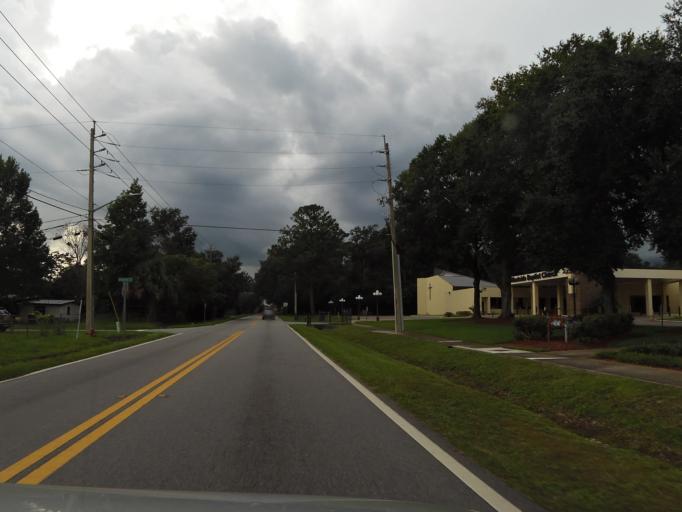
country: US
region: Florida
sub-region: Clay County
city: Bellair-Meadowbrook Terrace
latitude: 30.2844
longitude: -81.7758
